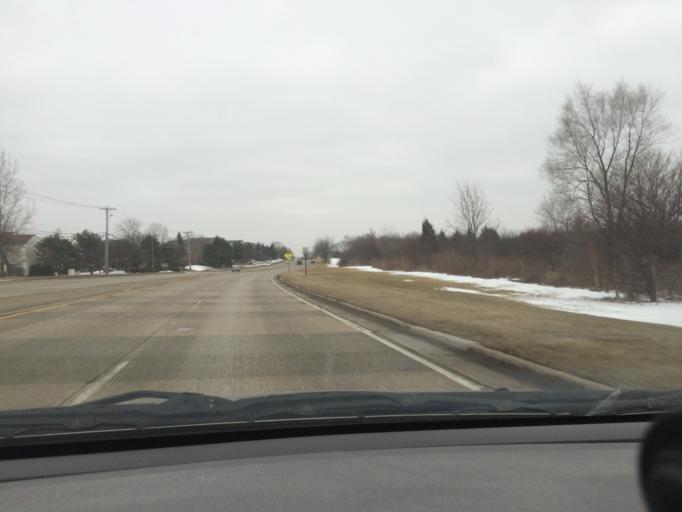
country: US
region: Illinois
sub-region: Cook County
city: Streamwood
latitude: 42.0367
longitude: -88.1791
